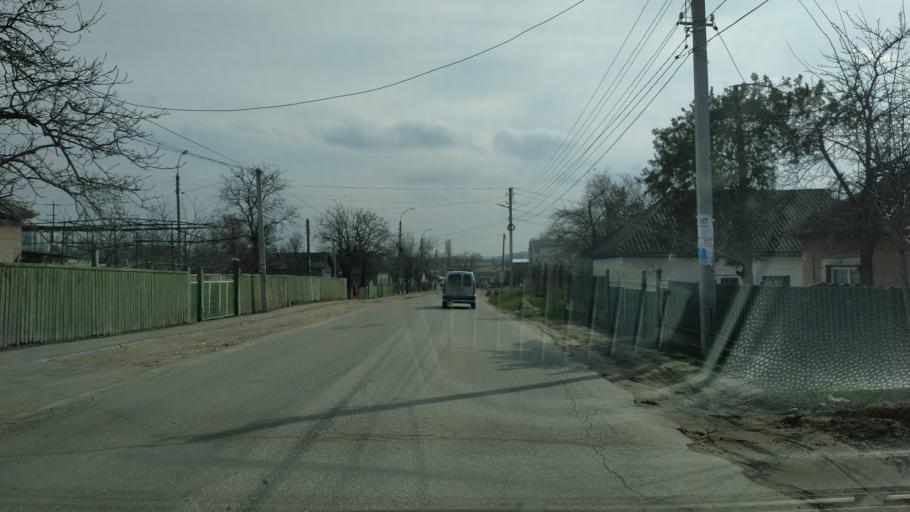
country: MD
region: Gagauzia
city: Vulcanesti
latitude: 45.6907
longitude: 28.4055
